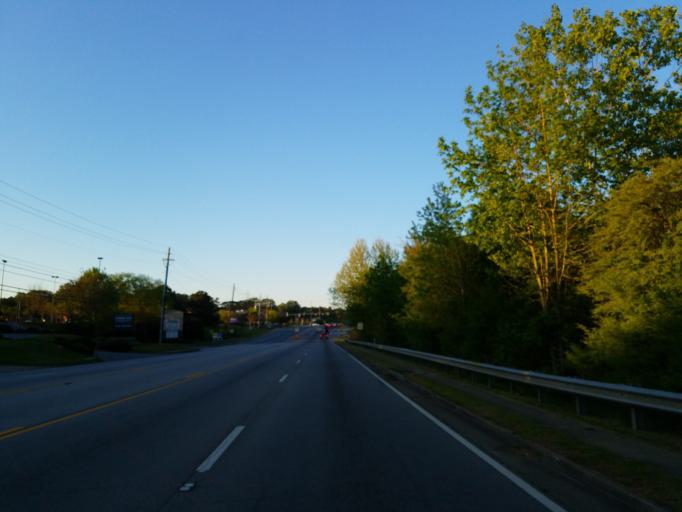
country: US
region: Georgia
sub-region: Cobb County
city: Fair Oaks
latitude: 33.9022
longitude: -84.6054
